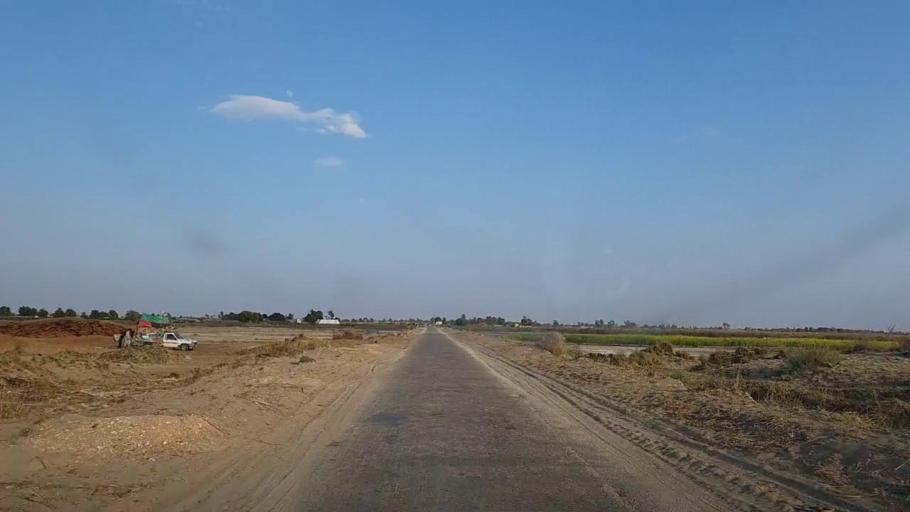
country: PK
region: Sindh
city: Sanghar
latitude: 26.2644
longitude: 68.9487
